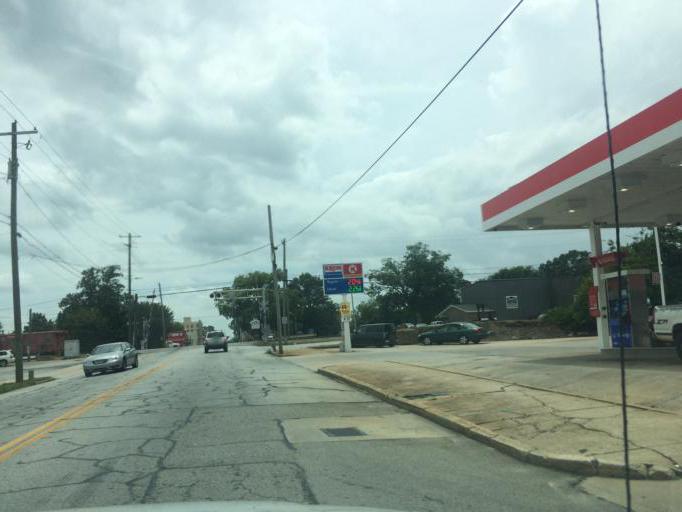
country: US
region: Georgia
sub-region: Elbert County
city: Elberton
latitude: 34.1136
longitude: -82.8661
